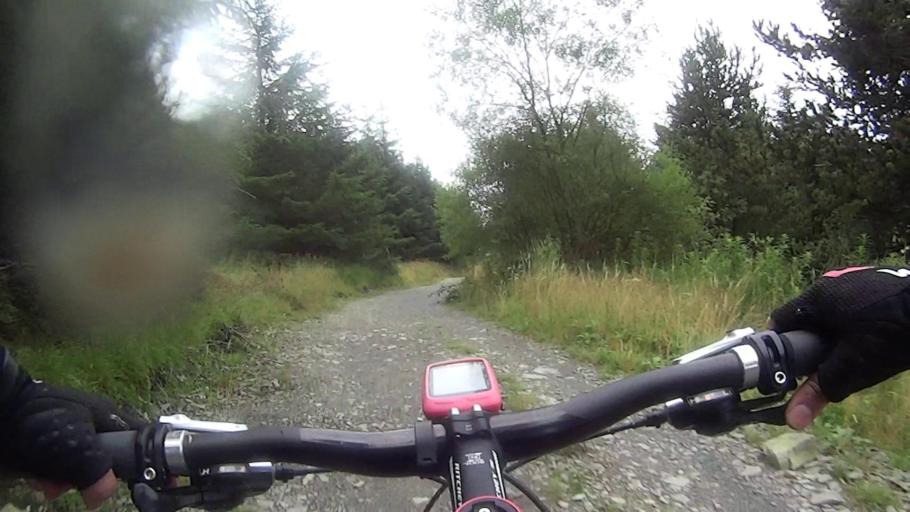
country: GB
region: Wales
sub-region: County of Ceredigion
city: Bow Street
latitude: 52.4226
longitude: -3.8806
